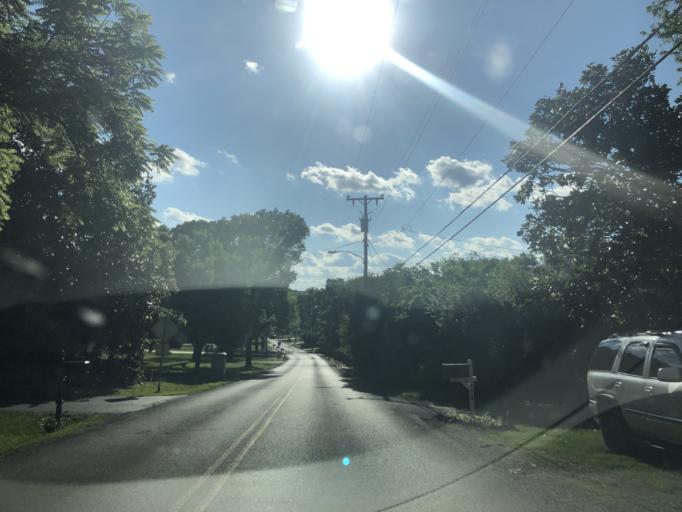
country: US
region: Tennessee
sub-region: Davidson County
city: Oak Hill
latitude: 36.0971
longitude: -86.8153
